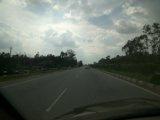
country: IN
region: Karnataka
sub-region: Kolar
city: Kolar
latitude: 13.1220
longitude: 78.0705
